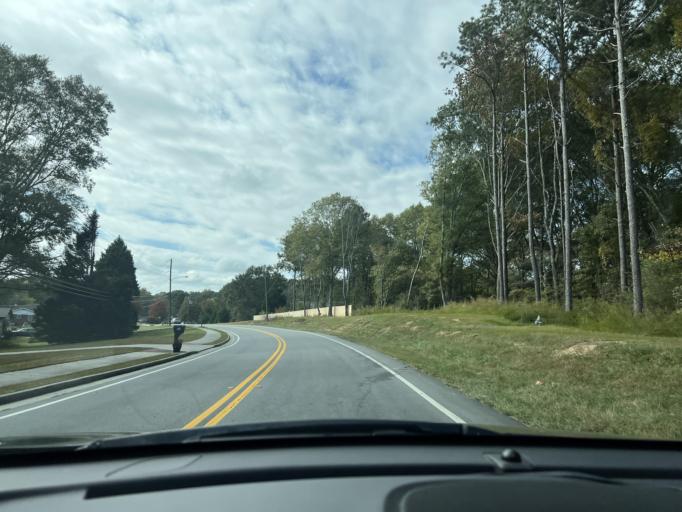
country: US
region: Georgia
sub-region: Gwinnett County
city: Grayson
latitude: 33.8999
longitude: -83.9504
